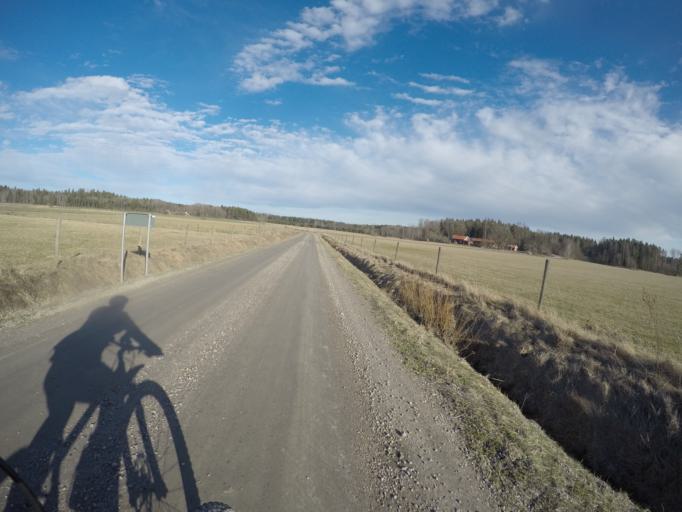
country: SE
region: Soedermanland
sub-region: Eskilstuna Kommun
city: Kvicksund
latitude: 59.4213
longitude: 16.2314
